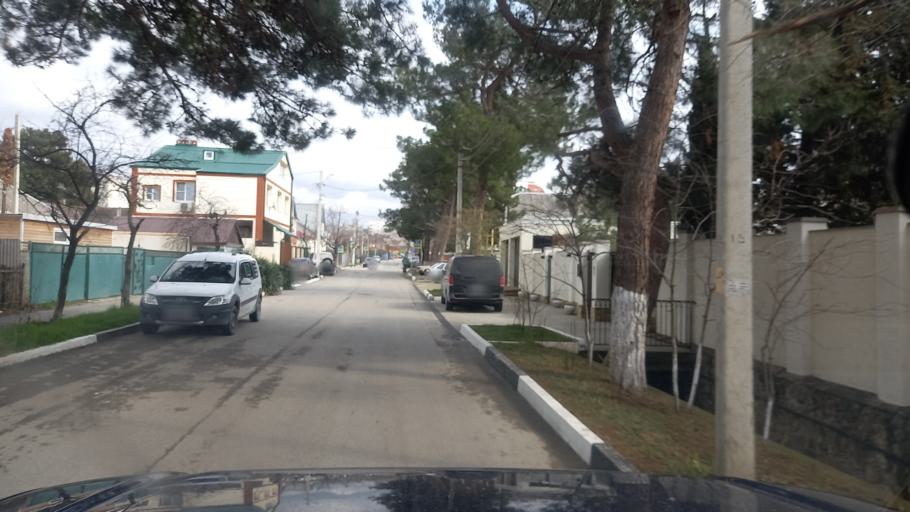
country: RU
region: Krasnodarskiy
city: Gelendzhik
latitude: 44.5587
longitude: 38.0890
